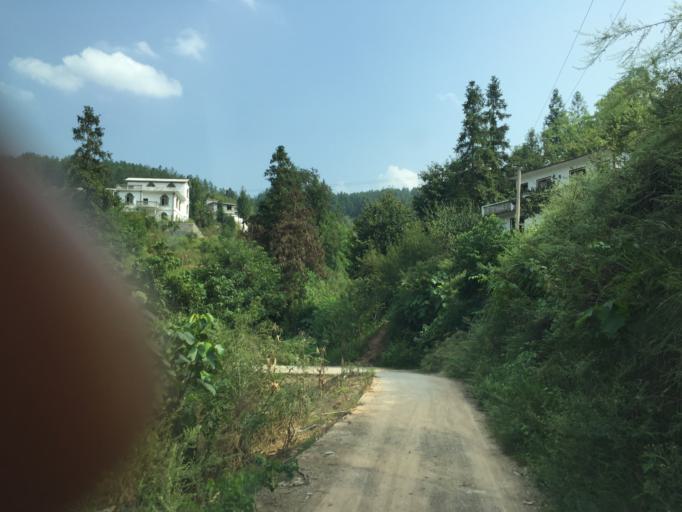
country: CN
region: Guizhou Sheng
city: Jingjiao
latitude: 28.3621
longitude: 108.1174
